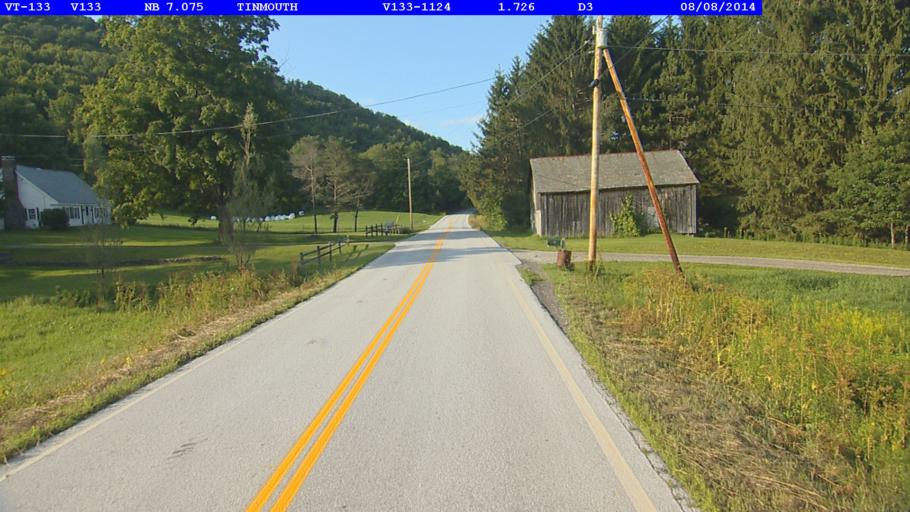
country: US
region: New York
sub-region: Washington County
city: Granville
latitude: 43.4270
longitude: -73.1162
